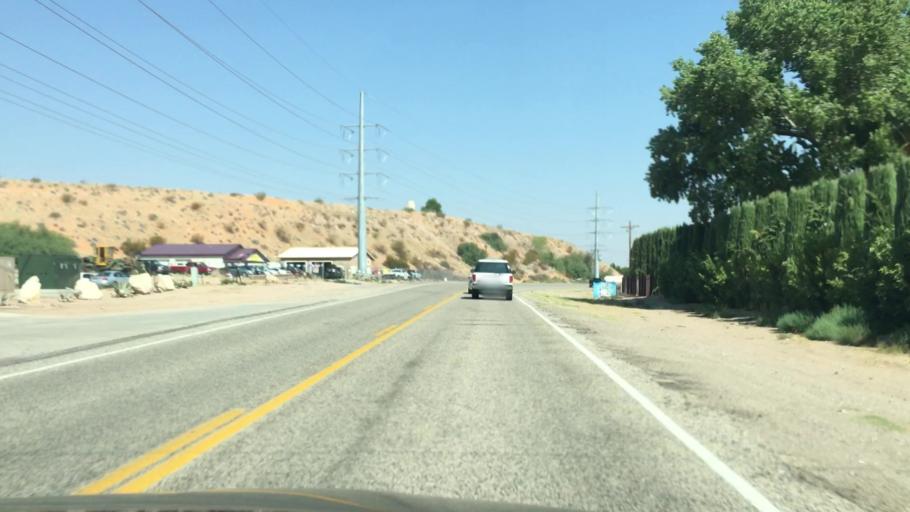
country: US
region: Arizona
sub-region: Mohave County
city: Beaver Dam
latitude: 36.8970
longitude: -113.9335
